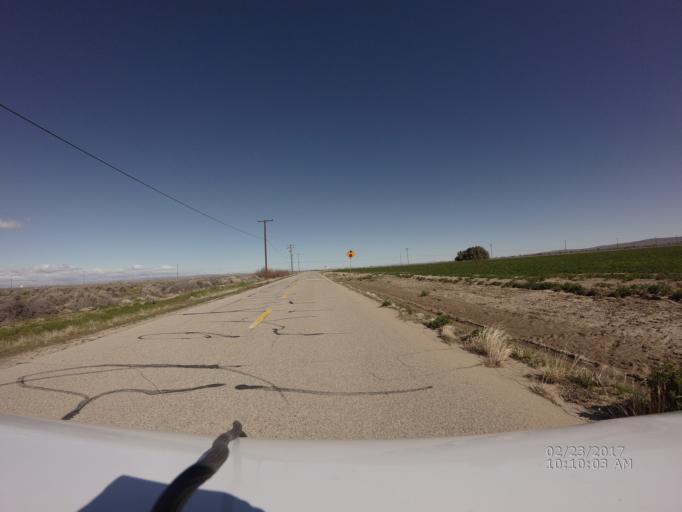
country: US
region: California
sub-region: Los Angeles County
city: Lake Los Angeles
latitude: 34.7177
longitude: -117.9341
